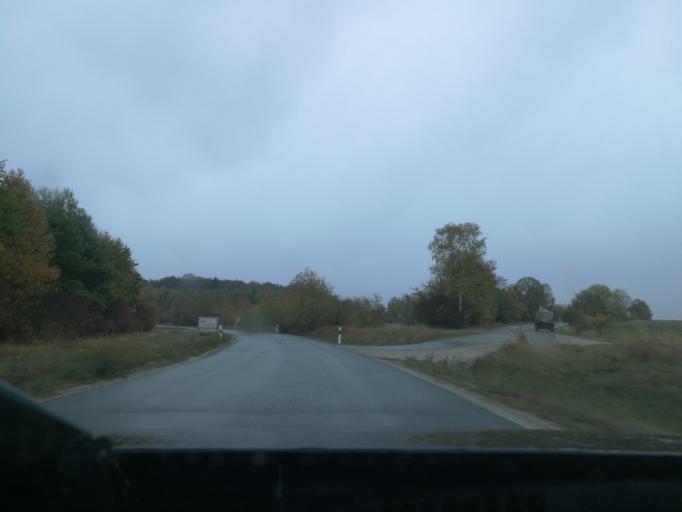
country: DE
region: Bavaria
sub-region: Regierungsbezirk Mittelfranken
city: Emskirchen
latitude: 49.5418
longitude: 10.7289
